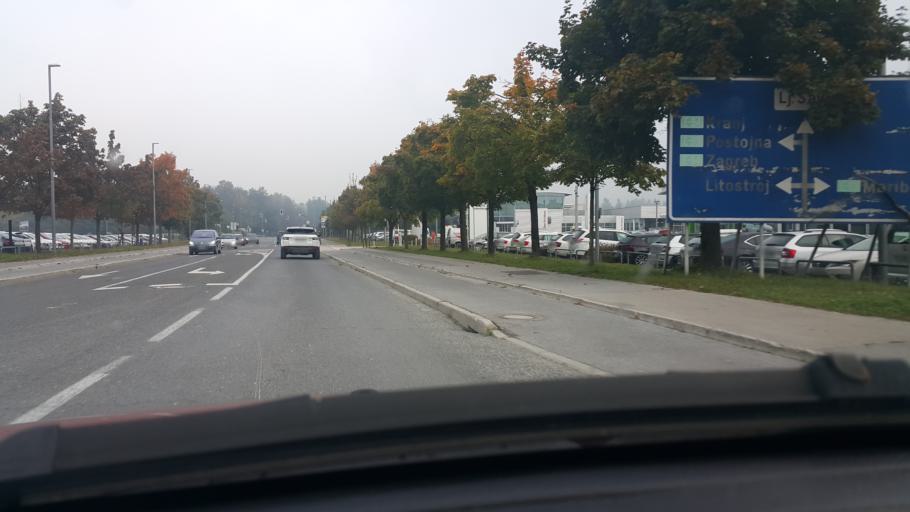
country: SI
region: Ljubljana
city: Ljubljana
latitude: 46.0824
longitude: 14.5019
